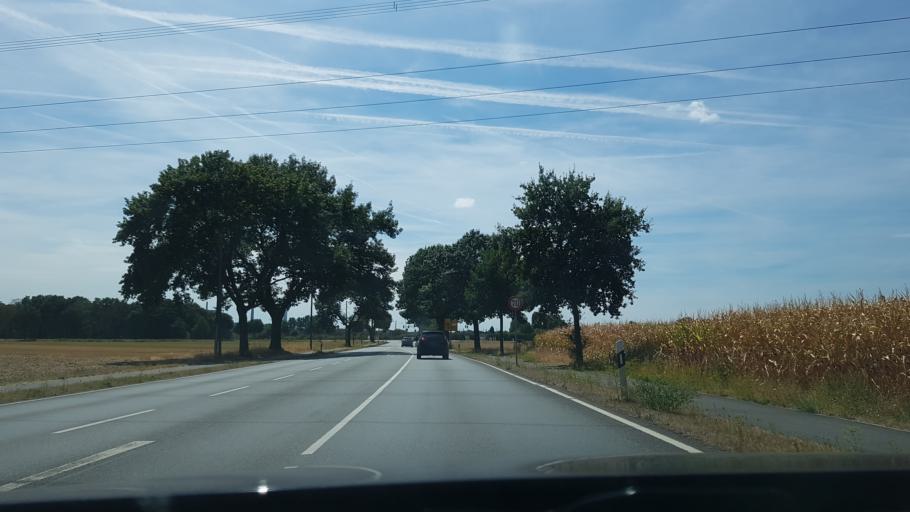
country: DE
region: North Rhine-Westphalia
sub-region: Regierungsbezirk Dusseldorf
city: Voerde
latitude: 51.6177
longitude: 6.6930
